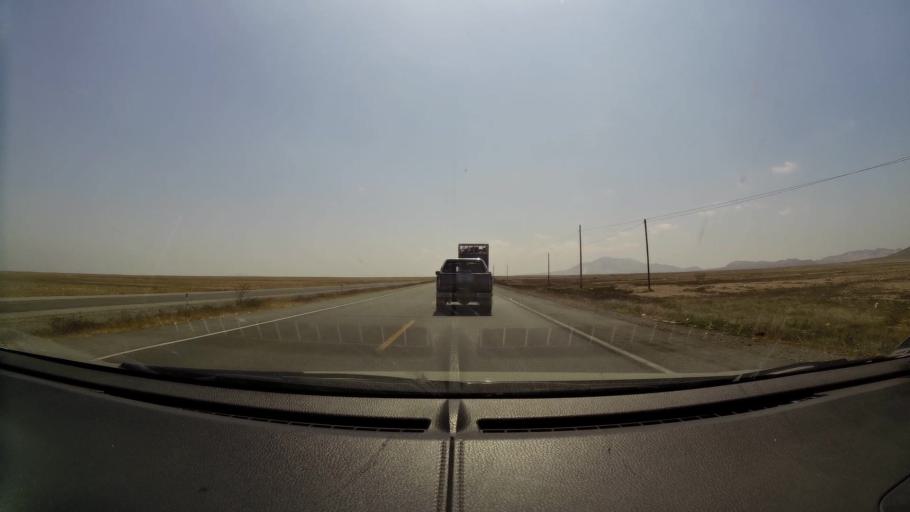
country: PE
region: Lambayeque
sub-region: Provincia de Chiclayo
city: Mocupe
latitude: -6.9535
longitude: -79.6995
